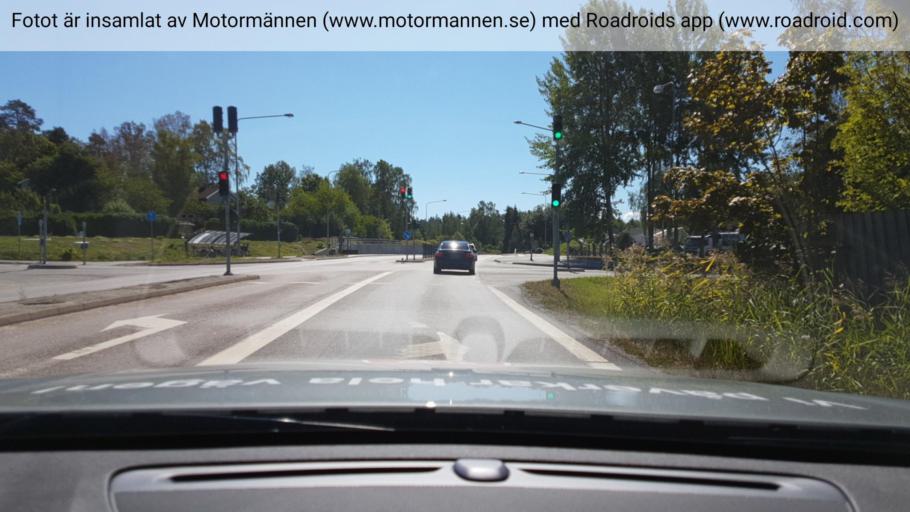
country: SE
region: Stockholm
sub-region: Tyreso Kommun
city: Bollmora
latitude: 59.2150
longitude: 18.2067
